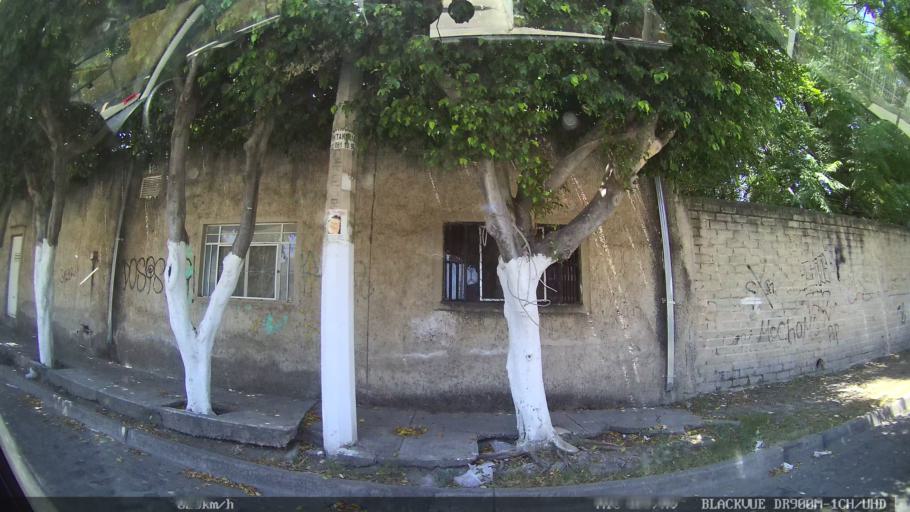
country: MX
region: Jalisco
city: Tlaquepaque
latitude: 20.6811
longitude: -103.2808
